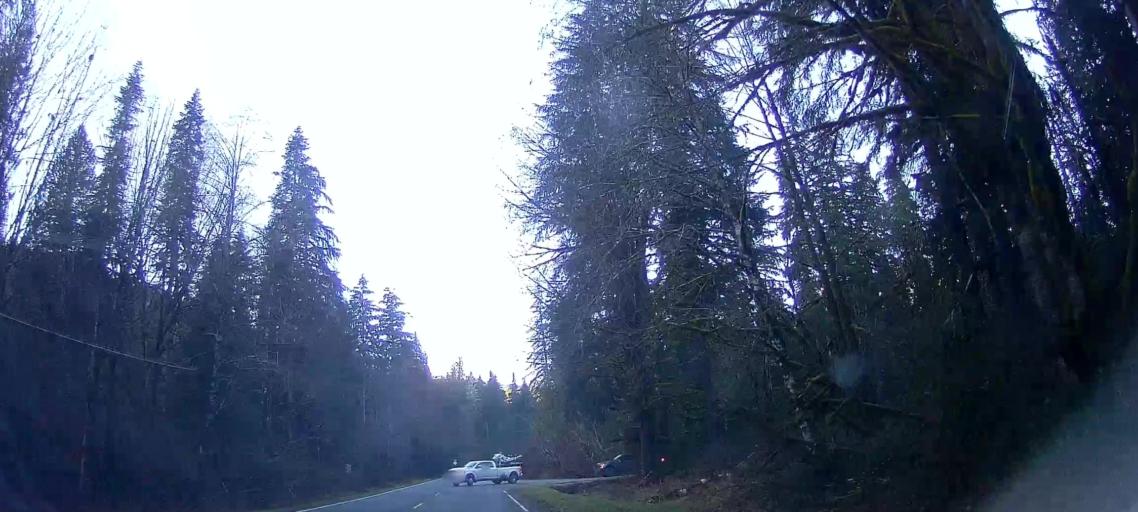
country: US
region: Washington
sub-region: Snohomish County
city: Darrington
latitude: 48.6628
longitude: -121.7167
